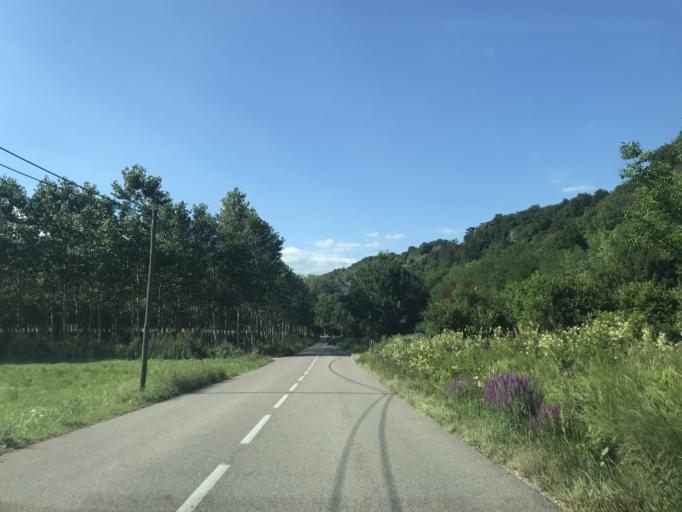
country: FR
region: Rhone-Alpes
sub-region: Departement de la Savoie
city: Yenne
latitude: 45.7467
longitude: 5.7919
